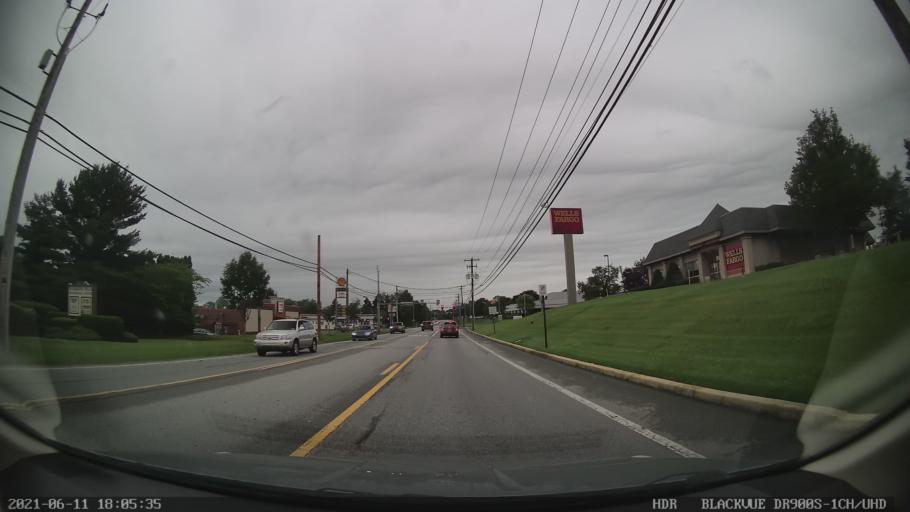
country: US
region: Pennsylvania
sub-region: Berks County
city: Wyomissing Hills
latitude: 40.3415
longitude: -75.9877
